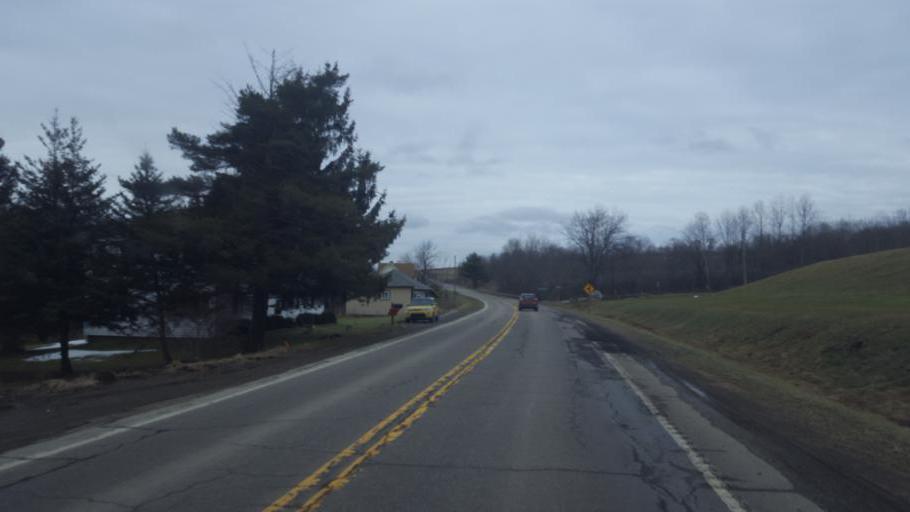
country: US
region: Pennsylvania
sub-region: Potter County
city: Galeton
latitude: 41.8796
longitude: -77.8150
